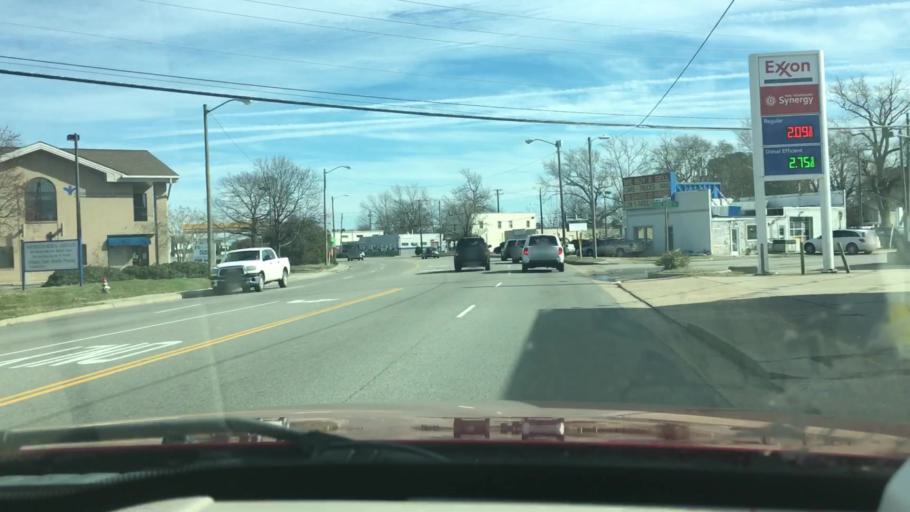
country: US
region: Virginia
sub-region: City of Portsmouth
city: Portsmouth Heights
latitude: 36.8350
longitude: -76.3465
